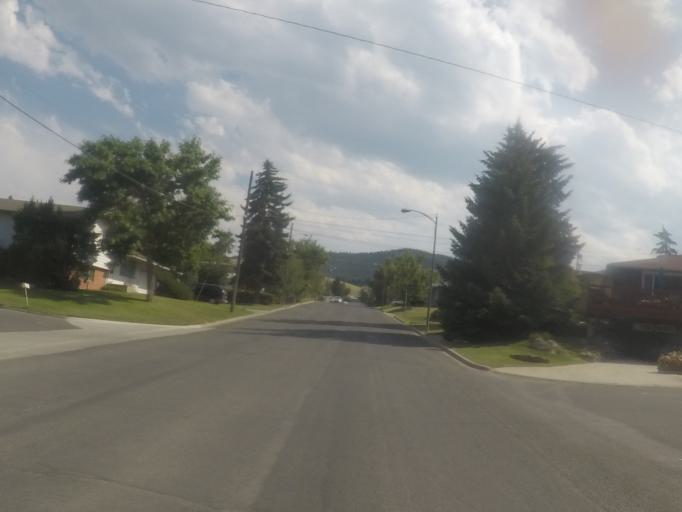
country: US
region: Montana
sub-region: Lewis and Clark County
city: Helena
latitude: 46.5852
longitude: -112.0072
